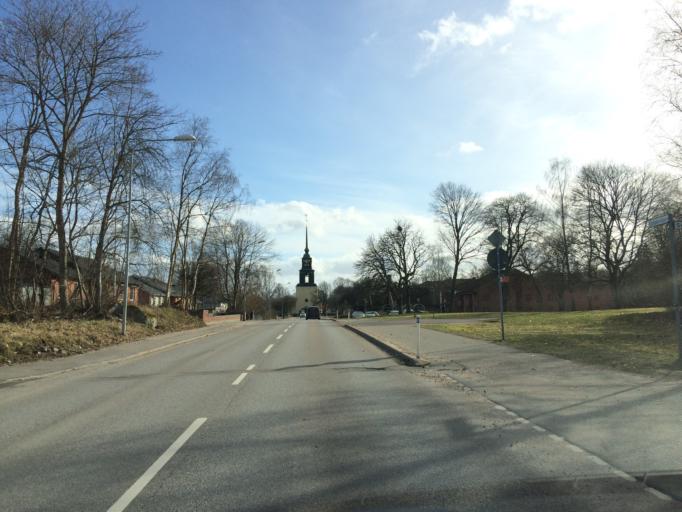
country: SE
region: Kronoberg
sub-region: Almhults Kommun
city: AElmhult
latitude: 56.5557
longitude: 14.1293
